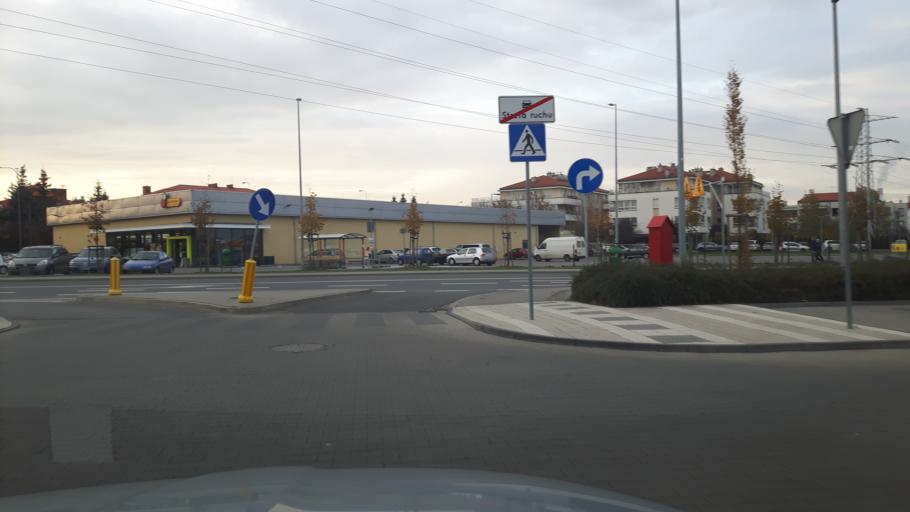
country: PL
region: Masovian Voivodeship
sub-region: Warszawa
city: Wilanow
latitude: 52.1659
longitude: 21.1104
